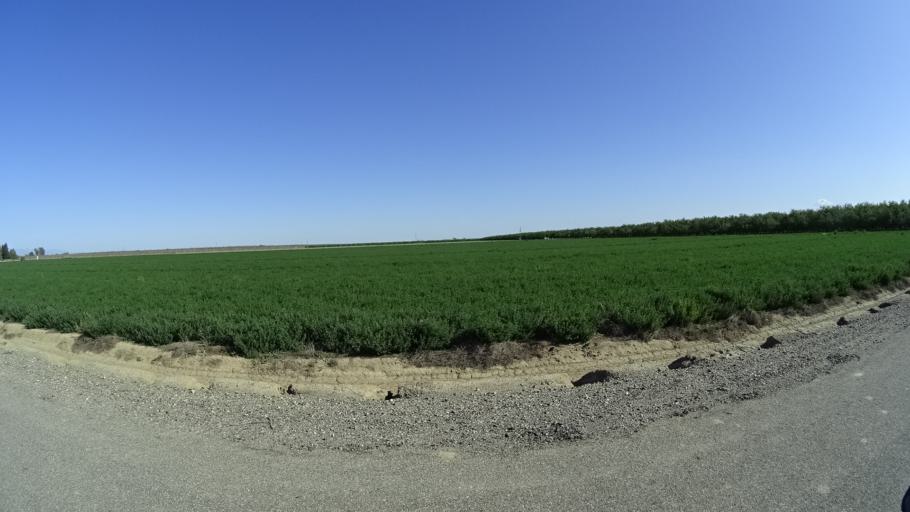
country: US
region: California
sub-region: Glenn County
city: Hamilton City
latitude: 39.6781
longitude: -122.0601
